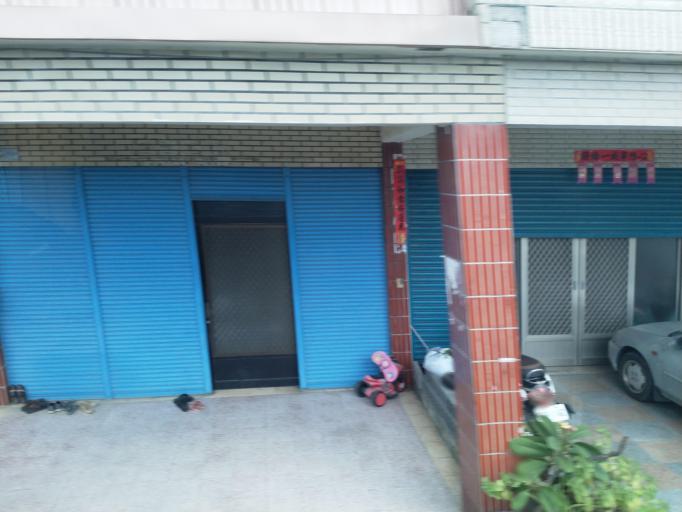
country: TW
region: Taiwan
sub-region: Pingtung
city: Pingtung
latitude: 22.8895
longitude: 120.5507
